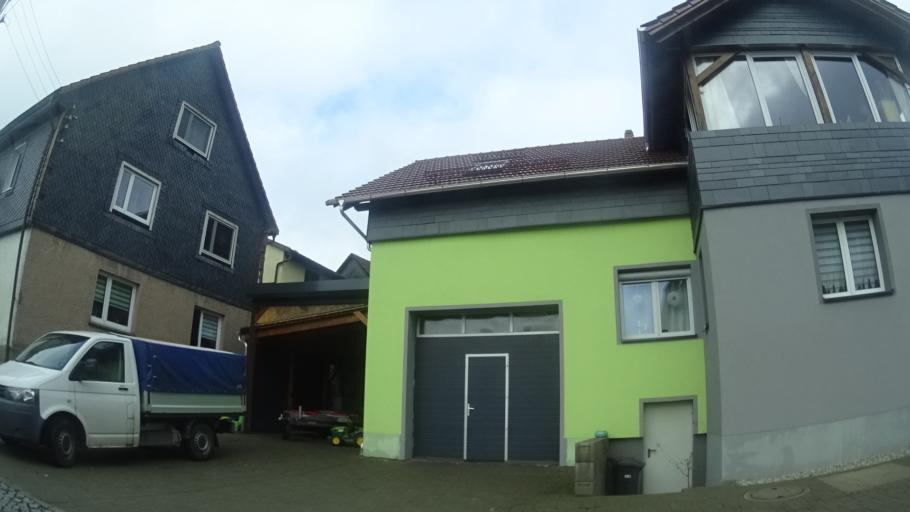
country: DE
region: Thuringia
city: Eisfeld
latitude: 50.4868
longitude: 10.8515
